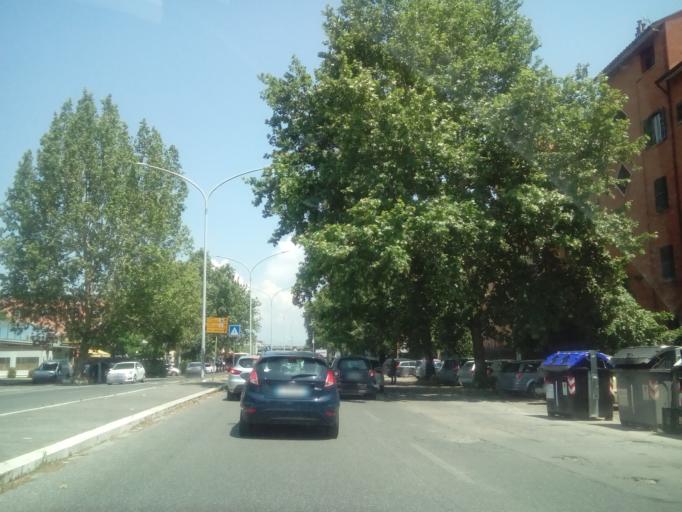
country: IT
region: Latium
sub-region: Citta metropolitana di Roma Capitale
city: Rome
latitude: 41.9110
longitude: 12.5501
